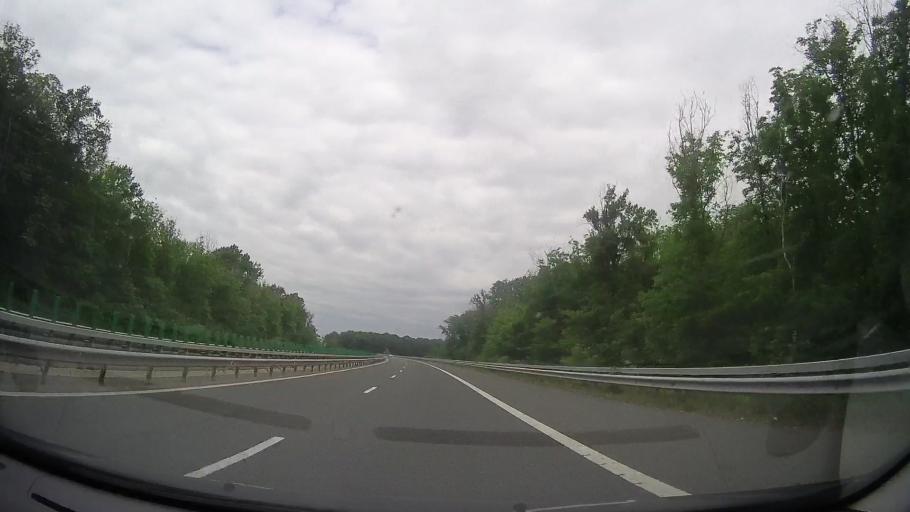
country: RO
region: Prahova
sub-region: Comuna Rafov
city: Rafov
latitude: 44.8849
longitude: 26.1313
